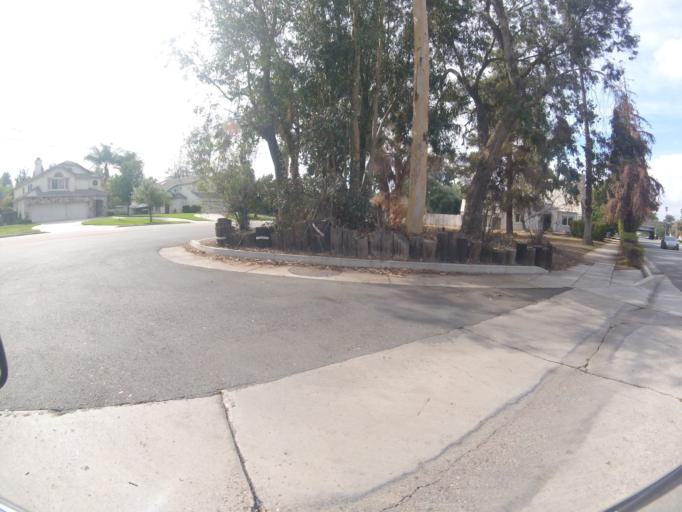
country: US
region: California
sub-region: San Bernardino County
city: Redlands
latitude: 34.0555
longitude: -117.1620
